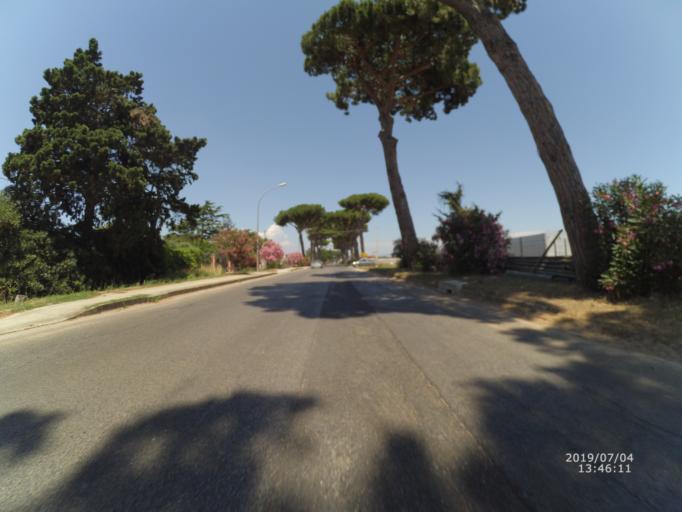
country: IT
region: Latium
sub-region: Provincia di Latina
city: San Felice Circeo
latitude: 41.2690
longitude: 13.0967
